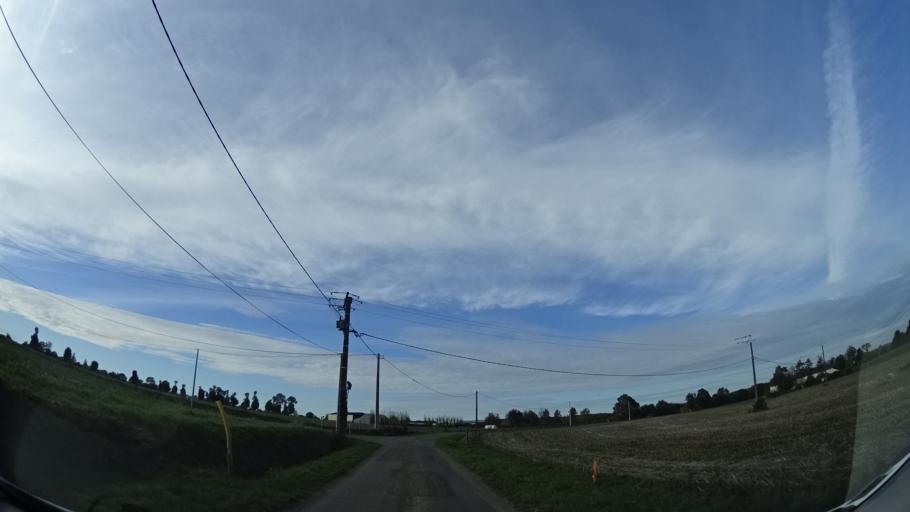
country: FR
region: Brittany
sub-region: Departement d'Ille-et-Vilaine
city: Geveze
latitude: 48.2390
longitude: -1.8284
